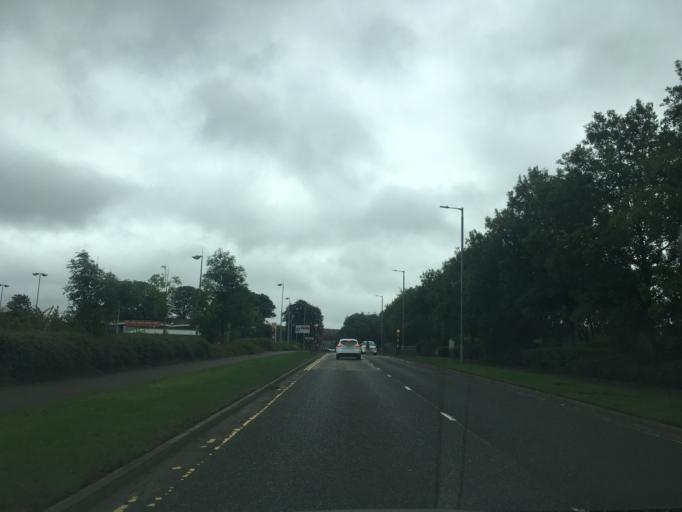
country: GB
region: Scotland
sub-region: Renfrewshire
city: Renfrew
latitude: 55.8719
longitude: -4.3586
